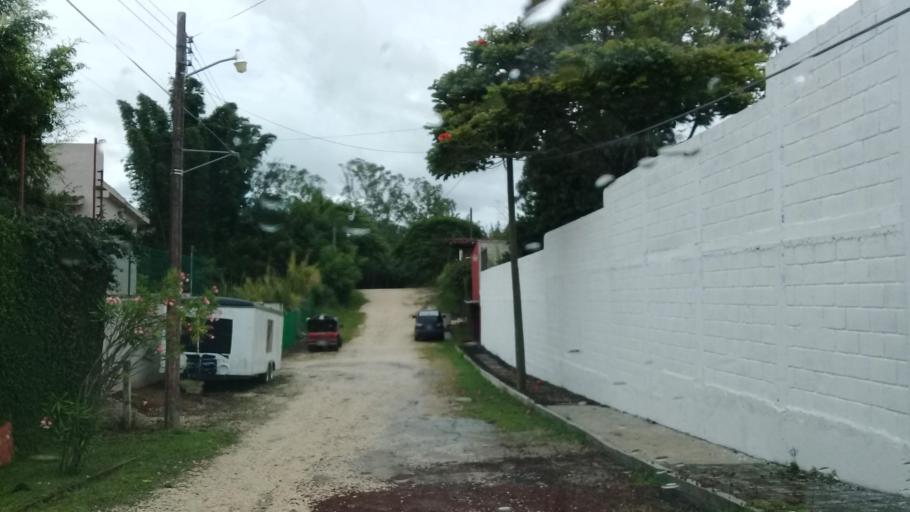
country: MX
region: Veracruz
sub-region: Emiliano Zapata
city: Jacarandas
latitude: 19.5057
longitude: -96.8395
